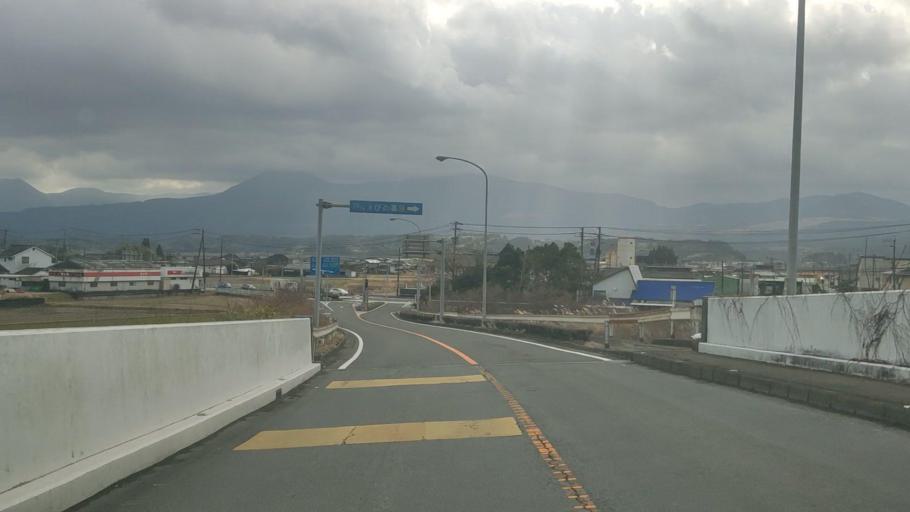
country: JP
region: Kumamoto
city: Hitoyoshi
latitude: 32.0540
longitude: 130.8170
